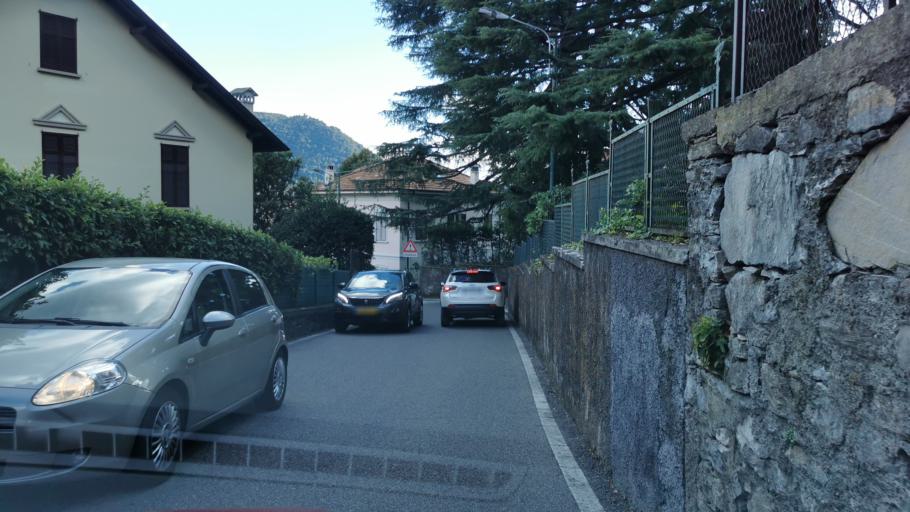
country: IT
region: Lombardy
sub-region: Provincia di Como
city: Cernobbio
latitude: 45.8449
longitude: 9.0752
